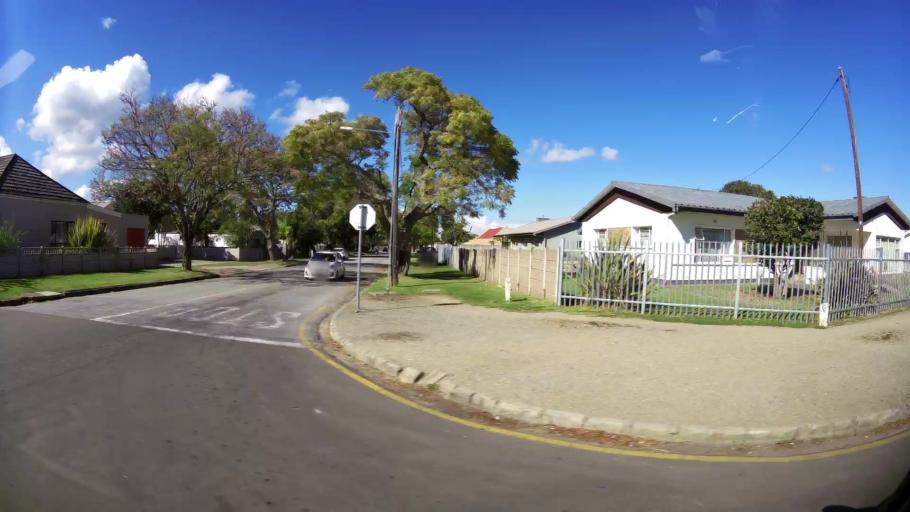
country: ZA
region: Western Cape
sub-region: Eden District Municipality
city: George
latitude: -33.9553
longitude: 22.4671
